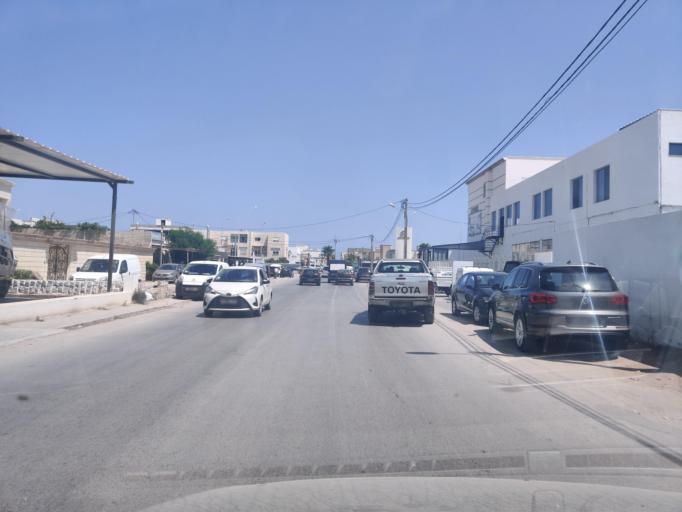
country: TN
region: Tunis
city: Al Marsa
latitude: 36.8753
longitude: 10.3072
